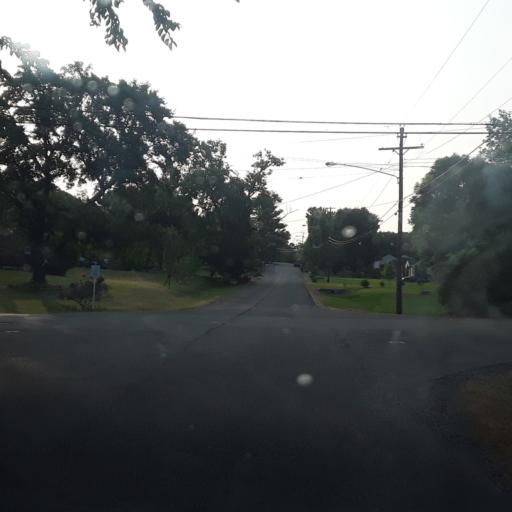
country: US
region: Tennessee
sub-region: Davidson County
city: Oak Hill
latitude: 36.0620
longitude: -86.7282
